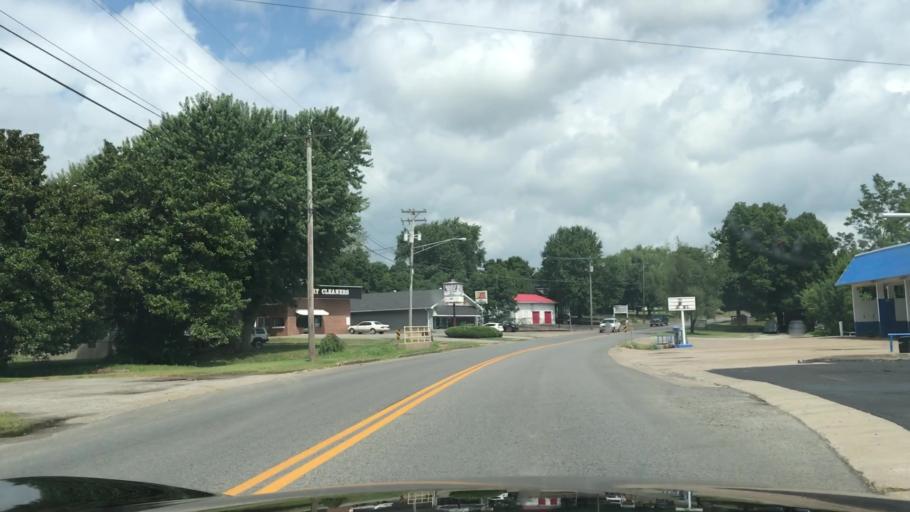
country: US
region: Kentucky
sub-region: Muhlenberg County
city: Greenville
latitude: 37.2090
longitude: -87.1803
